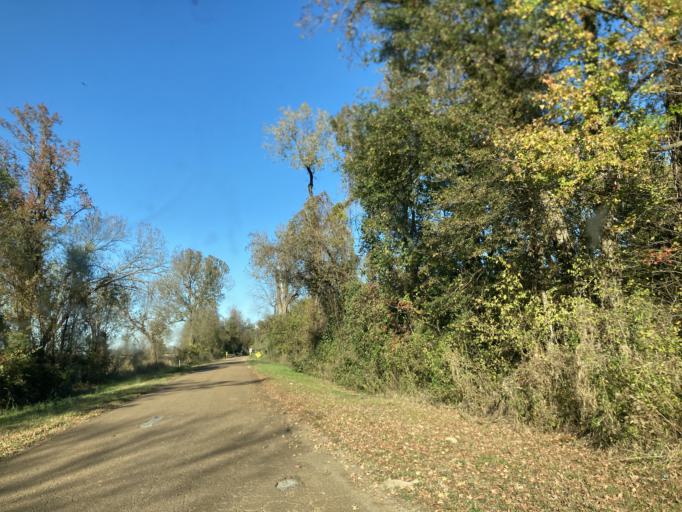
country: US
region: Mississippi
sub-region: Yazoo County
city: Yazoo City
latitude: 32.8145
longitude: -90.4502
